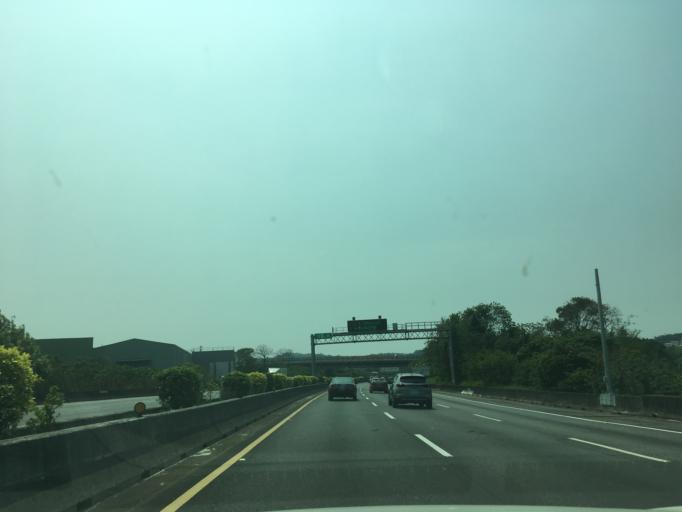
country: TW
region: Taiwan
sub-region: Miaoli
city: Miaoli
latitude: 24.6519
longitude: 120.8806
